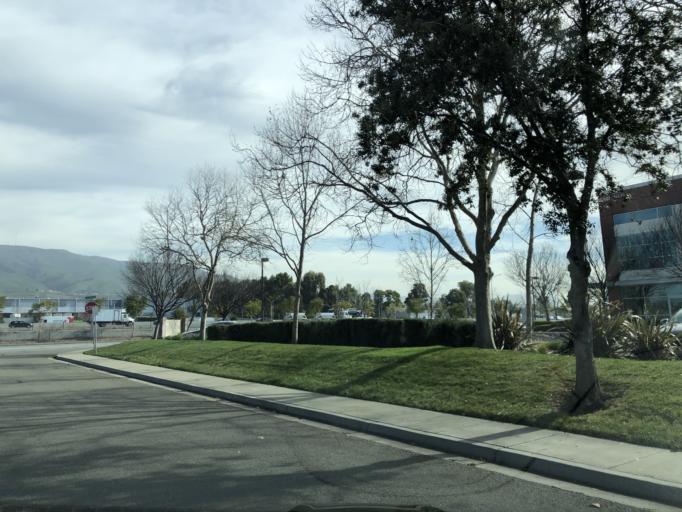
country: US
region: California
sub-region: Santa Clara County
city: Milpitas
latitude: 37.4725
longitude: -121.9324
